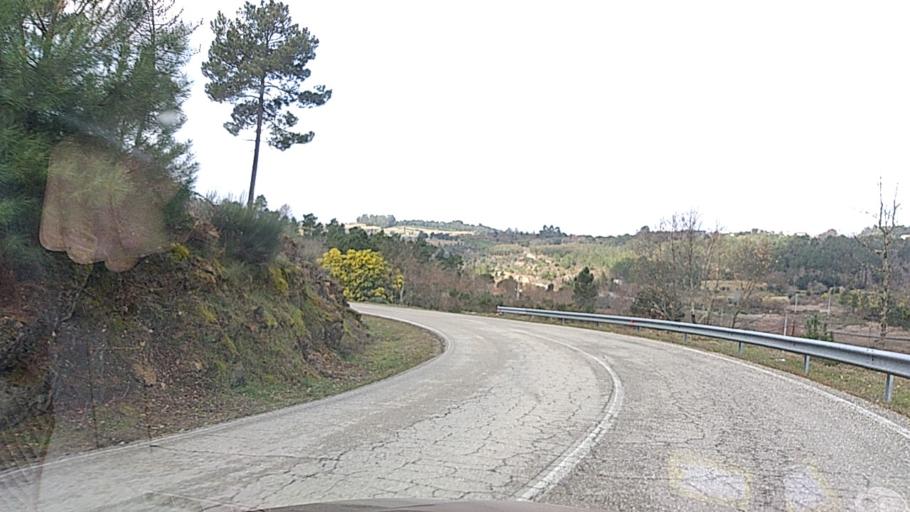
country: PT
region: Viseu
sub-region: Satao
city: Satao
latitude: 40.6642
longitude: -7.6763
